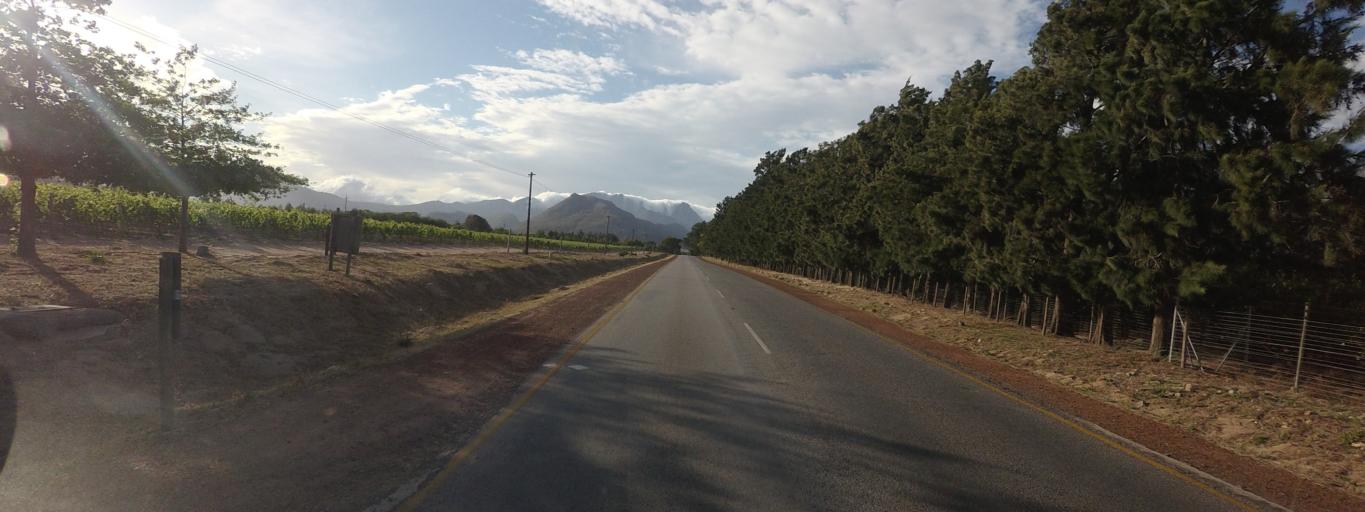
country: ZA
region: Western Cape
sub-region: Cape Winelands District Municipality
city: Paarl
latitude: -33.8663
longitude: 19.0412
